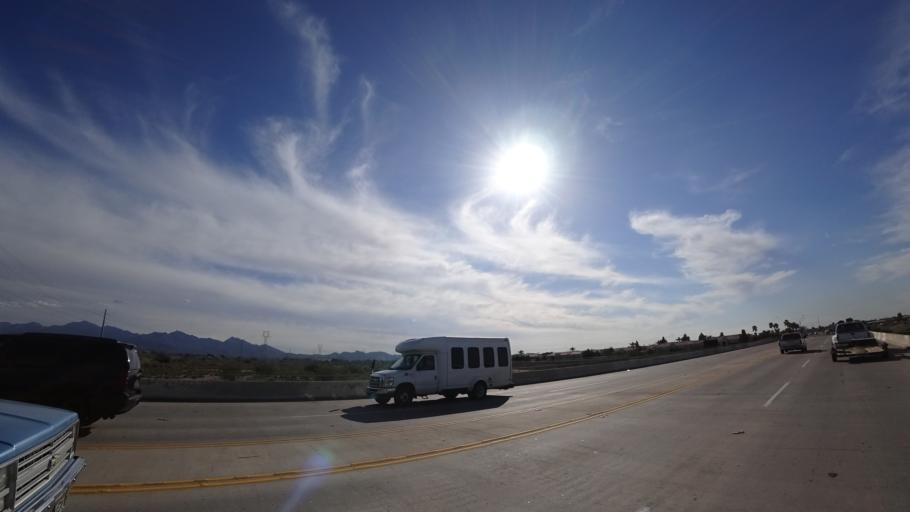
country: US
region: Arizona
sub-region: Maricopa County
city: Avondale
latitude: 33.4352
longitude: -112.3326
